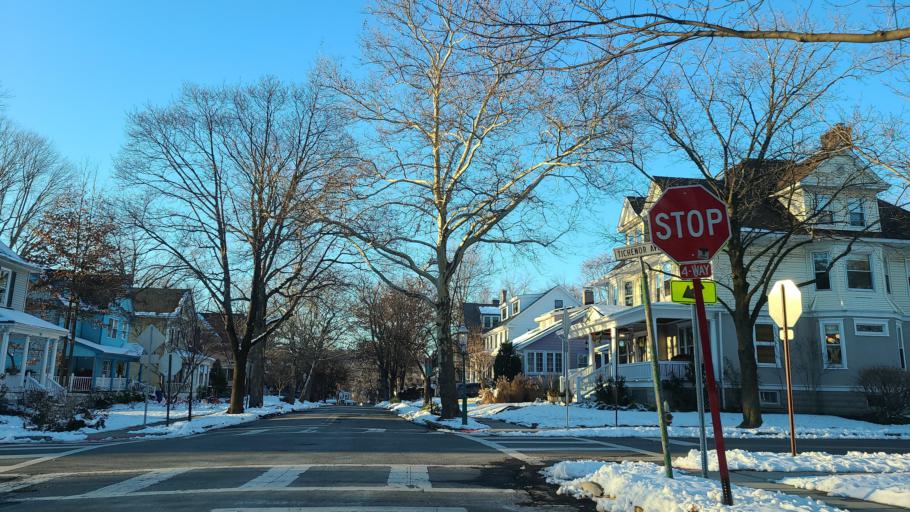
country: US
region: New Jersey
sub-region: Essex County
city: South Orange
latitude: 40.7406
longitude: -74.2562
